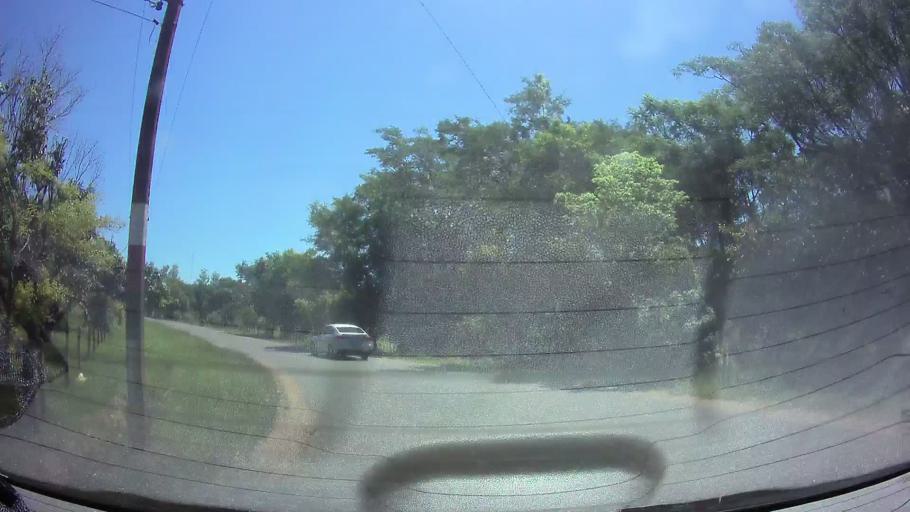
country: PY
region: Central
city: Aregua
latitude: -25.2632
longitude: -57.4225
